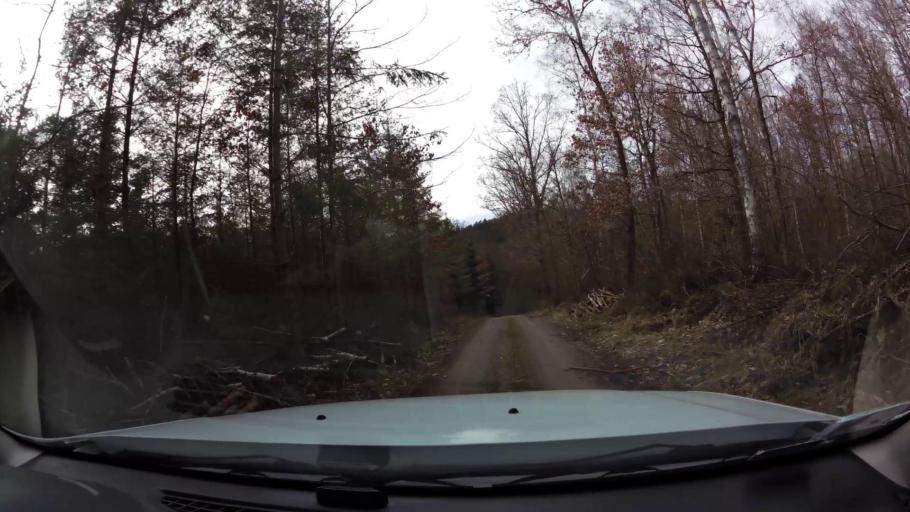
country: PL
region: West Pomeranian Voivodeship
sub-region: Powiat drawski
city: Drawsko Pomorskie
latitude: 53.5055
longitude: 15.7032
